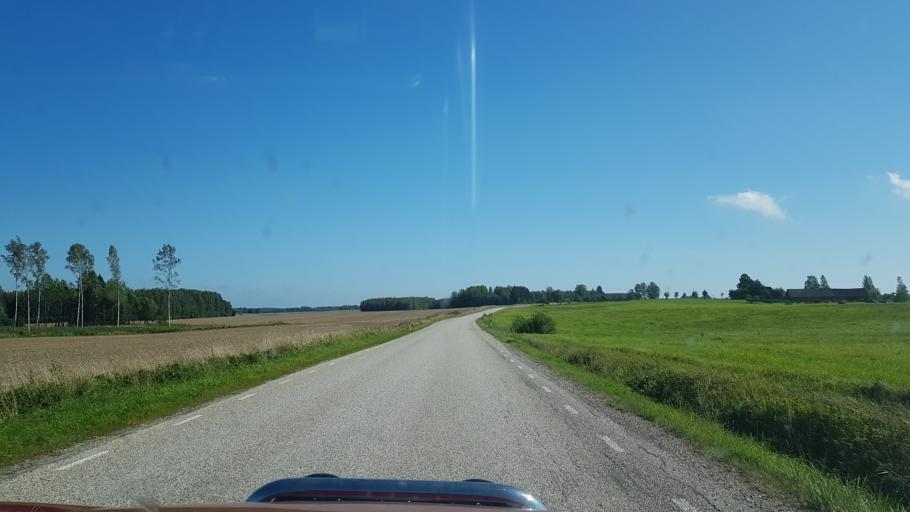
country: EE
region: Polvamaa
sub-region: Raepina vald
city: Rapina
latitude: 58.2338
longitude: 27.3375
